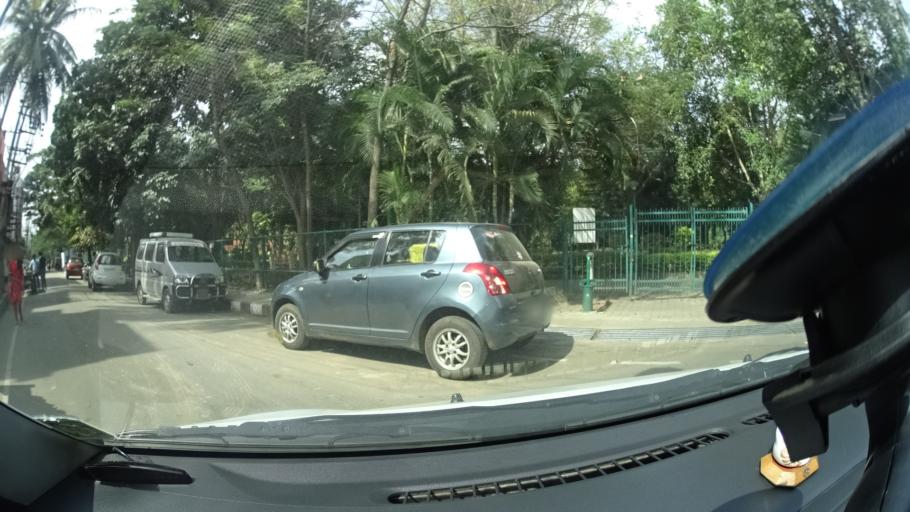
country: IN
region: Karnataka
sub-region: Bangalore Urban
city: Yelahanka
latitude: 13.0962
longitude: 77.5802
